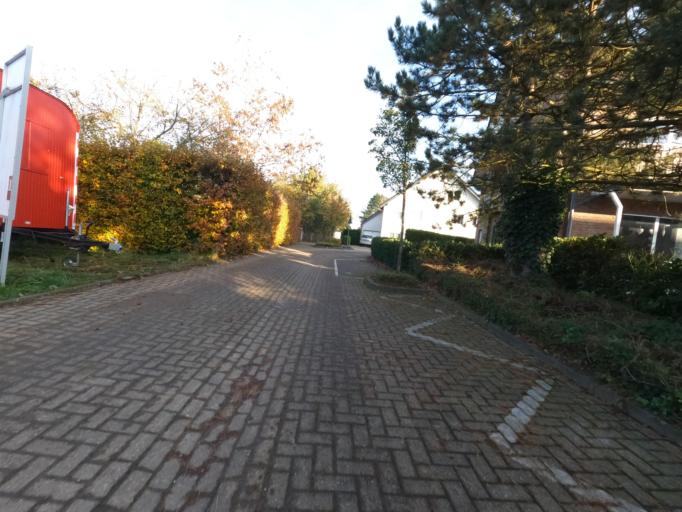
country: DE
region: North Rhine-Westphalia
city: Huckelhoven
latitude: 50.9974
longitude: 6.2120
